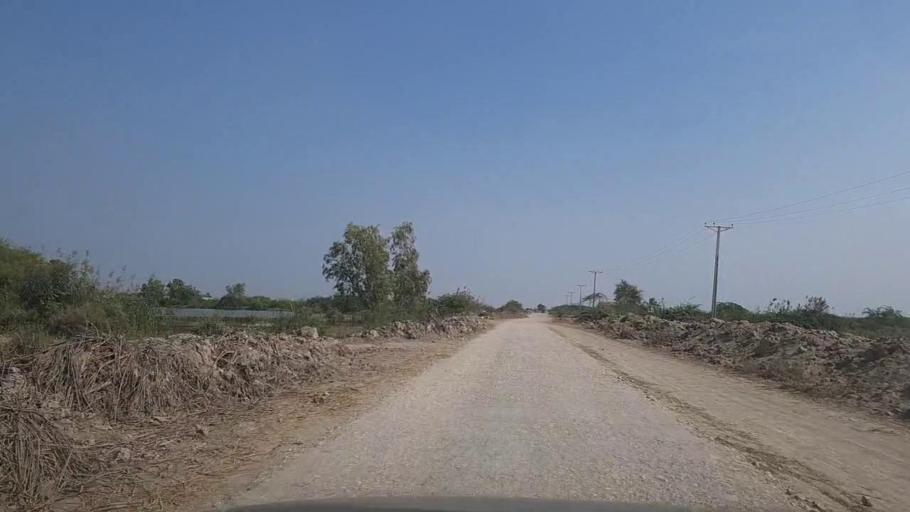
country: PK
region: Sindh
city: Thatta
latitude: 24.5837
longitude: 67.9043
